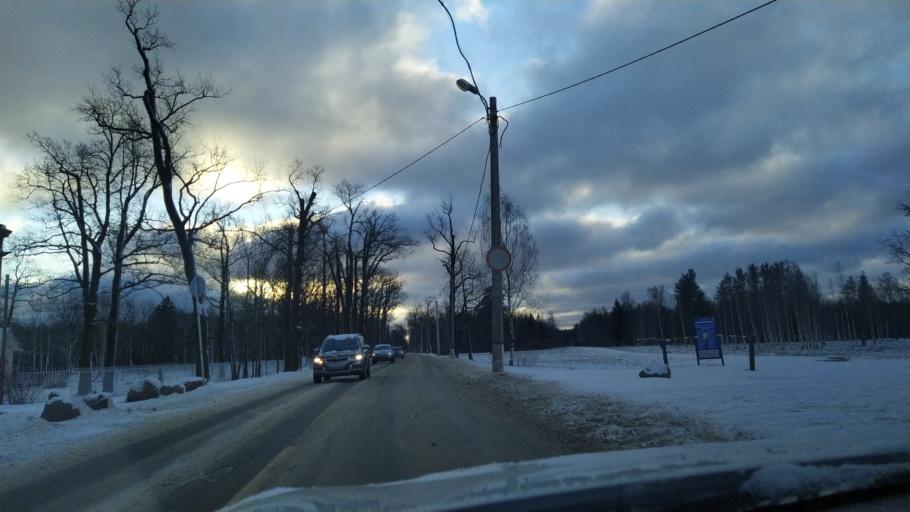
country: RU
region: St.-Petersburg
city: Aleksandrovskaya
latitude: 59.7278
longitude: 30.3564
